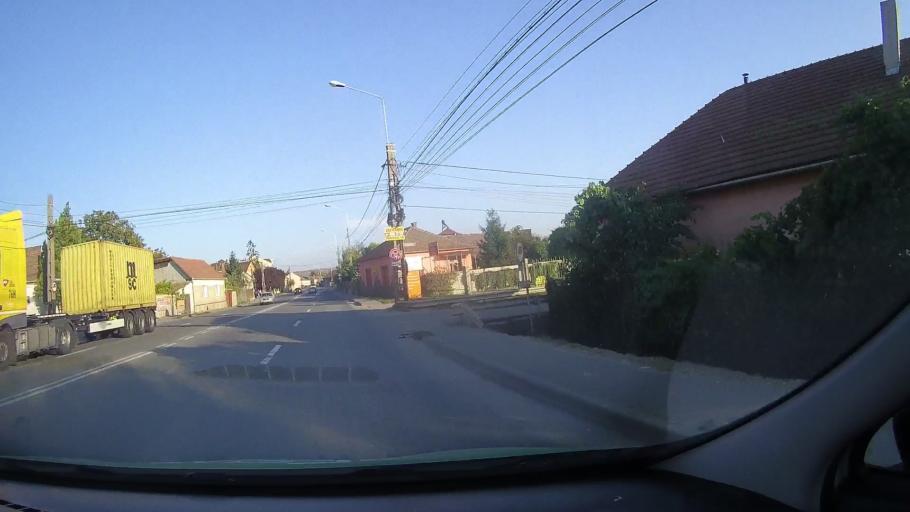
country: RO
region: Bihor
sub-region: Comuna Biharea
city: Biharea
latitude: 47.1026
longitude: 21.8962
